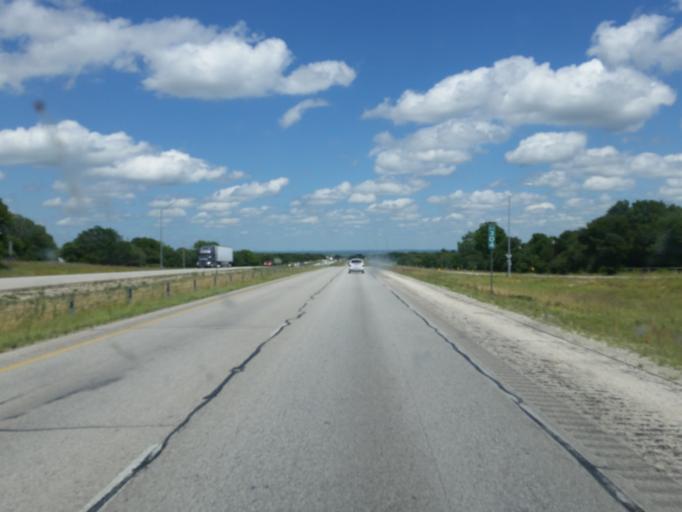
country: US
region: Texas
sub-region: Callahan County
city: Clyde
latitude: 32.4072
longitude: -99.4520
